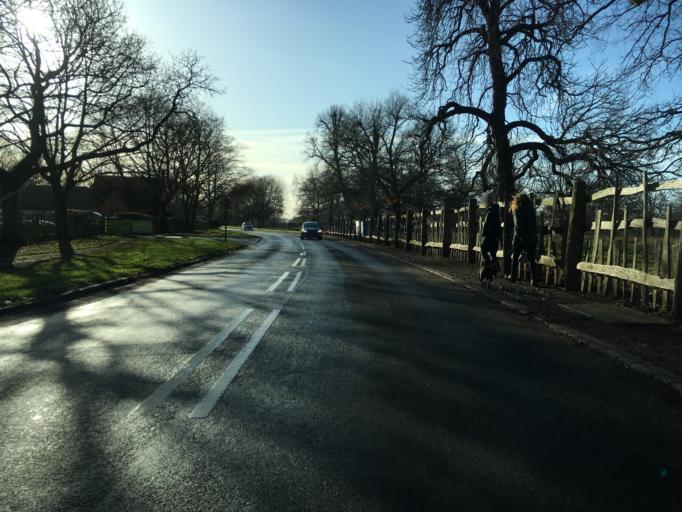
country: GB
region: England
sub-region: Warwickshire
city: Wellesbourne Mountford
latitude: 52.2062
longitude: -1.6170
